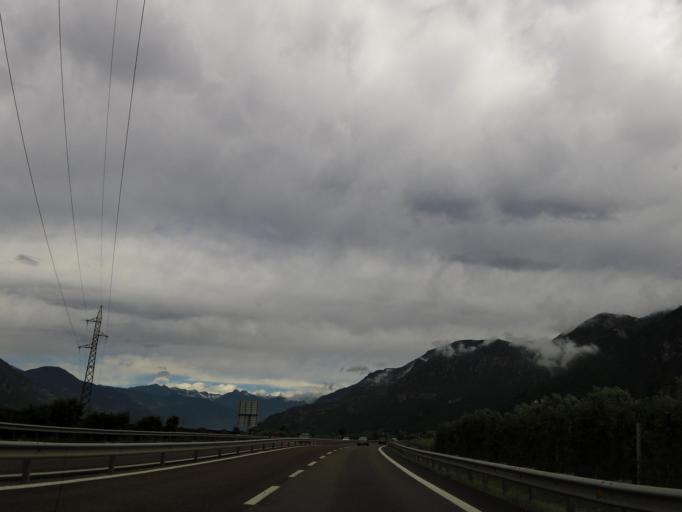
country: IT
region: Trentino-Alto Adige
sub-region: Bolzano
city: Cornaiano
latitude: 46.4888
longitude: 11.2869
